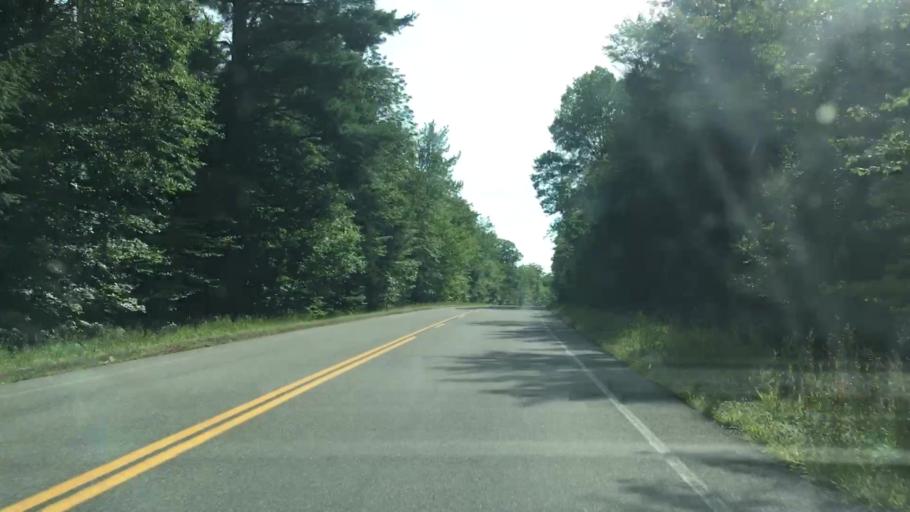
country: US
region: Maine
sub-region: Penobscot County
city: Lincoln
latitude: 45.3780
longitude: -68.5499
